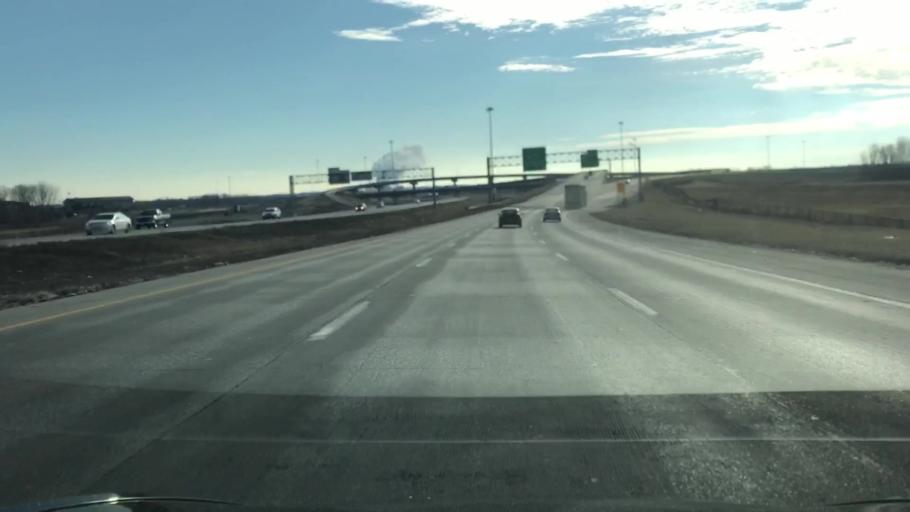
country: US
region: Nebraska
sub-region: Douglas County
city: Omaha
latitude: 41.2398
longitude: -95.9028
